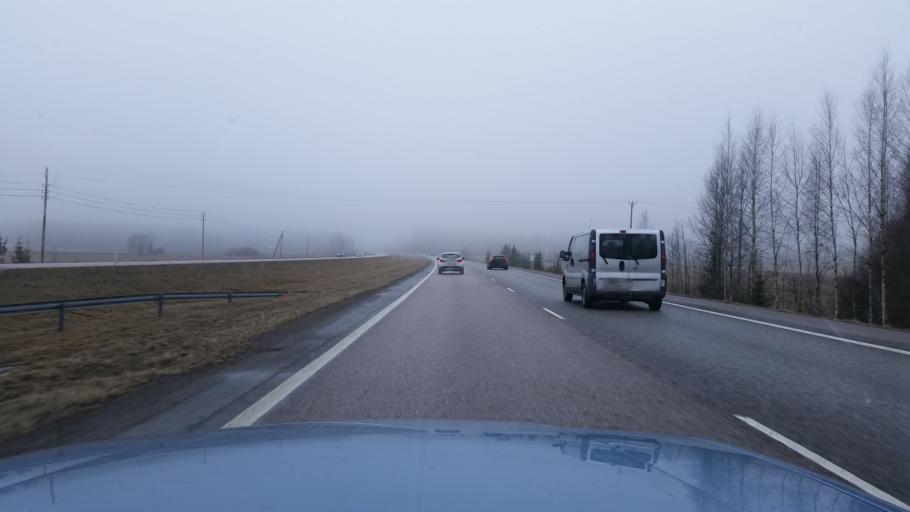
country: FI
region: Uusimaa
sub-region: Helsinki
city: Nurmijaervi
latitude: 60.4835
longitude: 24.8493
